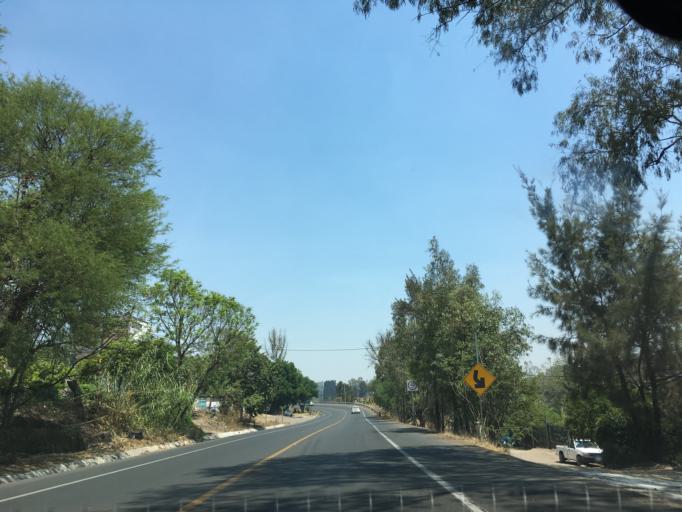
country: MX
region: Guanajuato
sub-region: Moroleon
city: Rinconadas del Bosque
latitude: 20.0983
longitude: -101.1599
